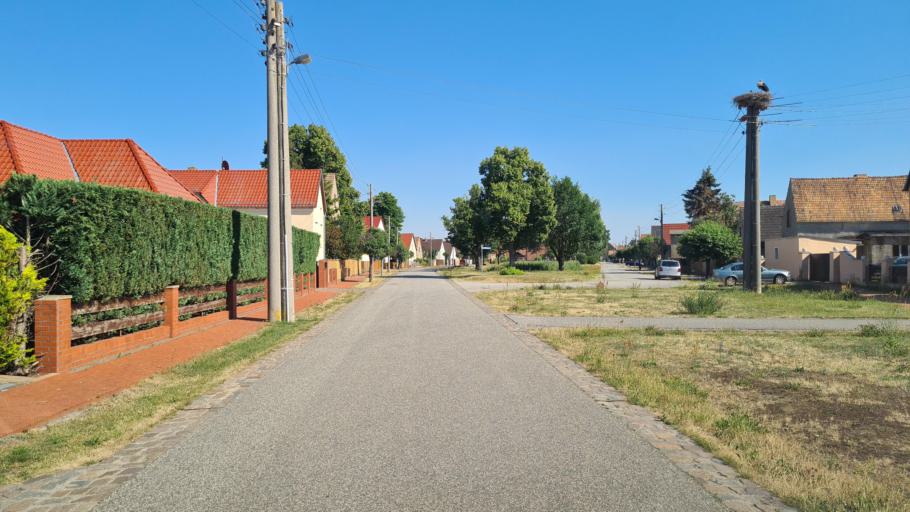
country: DE
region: Saxony-Anhalt
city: Annaburg
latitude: 51.6990
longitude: 12.9928
